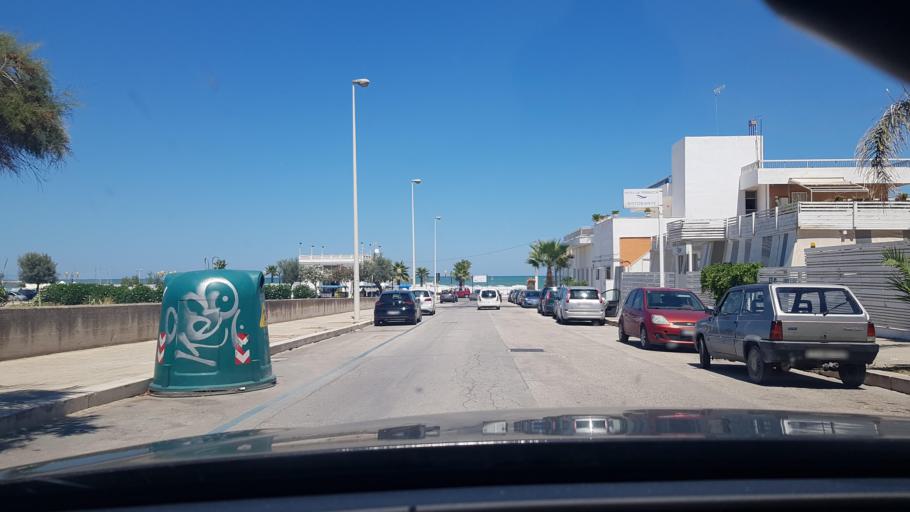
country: IT
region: Apulia
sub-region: Provincia di Barletta - Andria - Trani
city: Barletta
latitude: 41.3188
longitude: 16.2990
